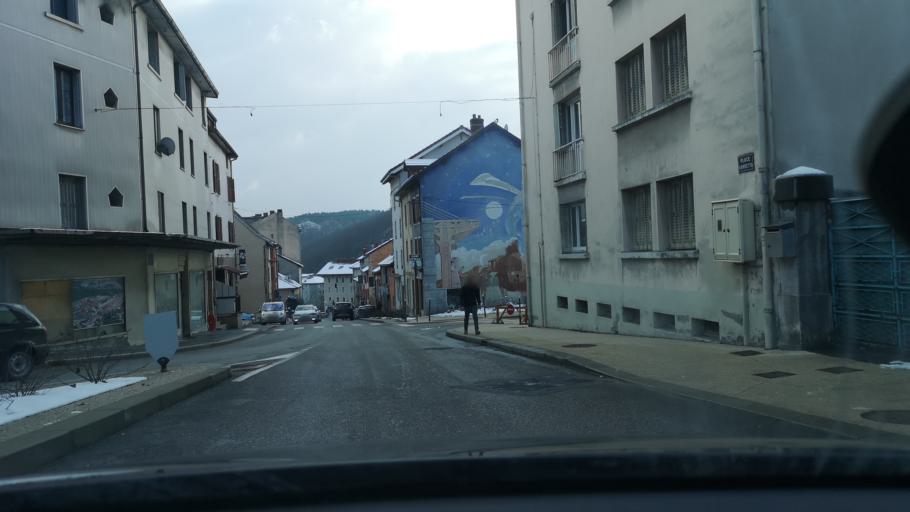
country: FR
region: Rhone-Alpes
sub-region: Departement de l'Ain
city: Bellegarde-sur-Valserine
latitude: 46.1097
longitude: 5.8279
